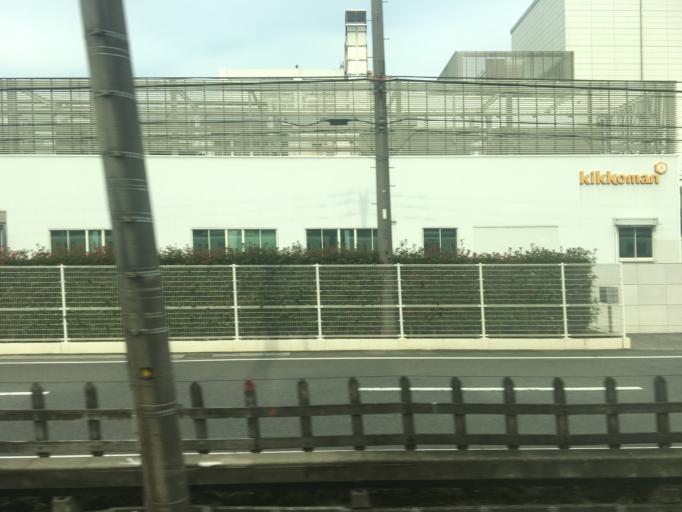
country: JP
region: Saitama
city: Sayama
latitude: 35.8815
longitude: 139.4432
